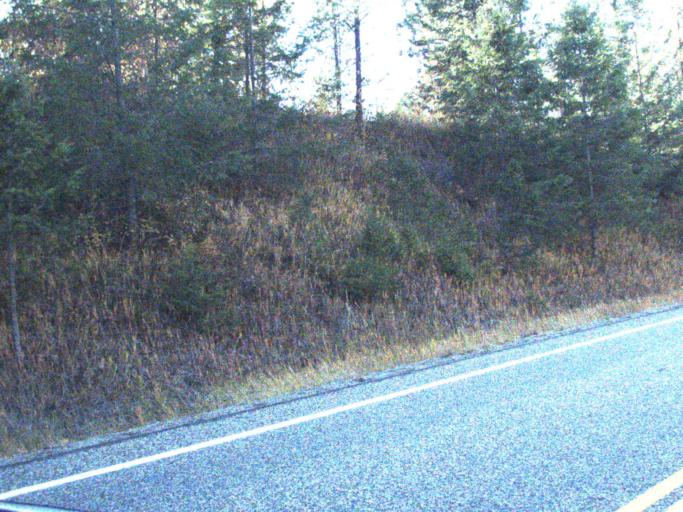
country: CA
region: British Columbia
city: Rossland
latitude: 48.9589
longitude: -117.8020
